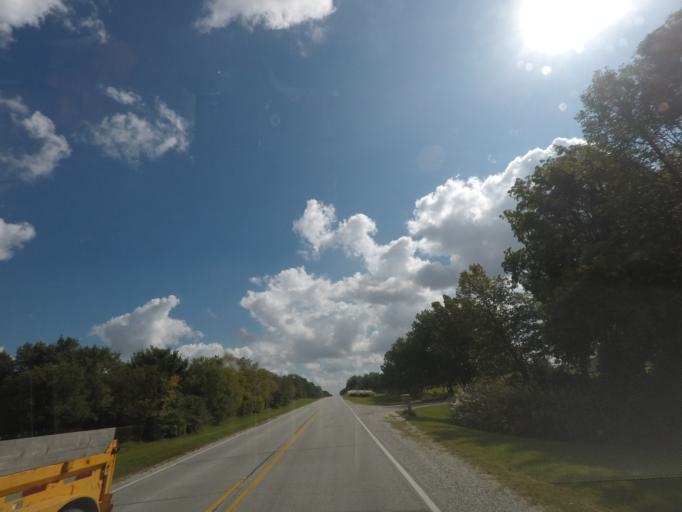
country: US
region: Iowa
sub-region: Story County
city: Nevada
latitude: 42.0227
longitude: -93.3835
